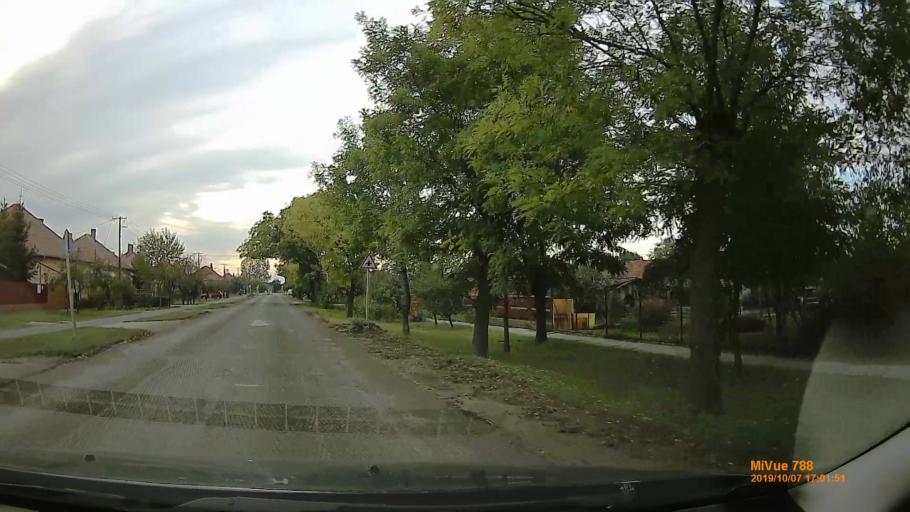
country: HU
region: Bekes
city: Szarvas
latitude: 46.8514
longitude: 20.5606
